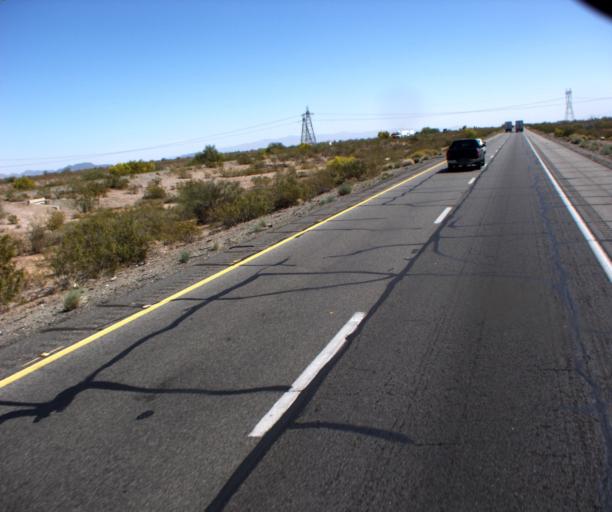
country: US
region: Arizona
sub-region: Maricopa County
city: Buckeye
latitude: 33.5150
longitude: -113.0385
